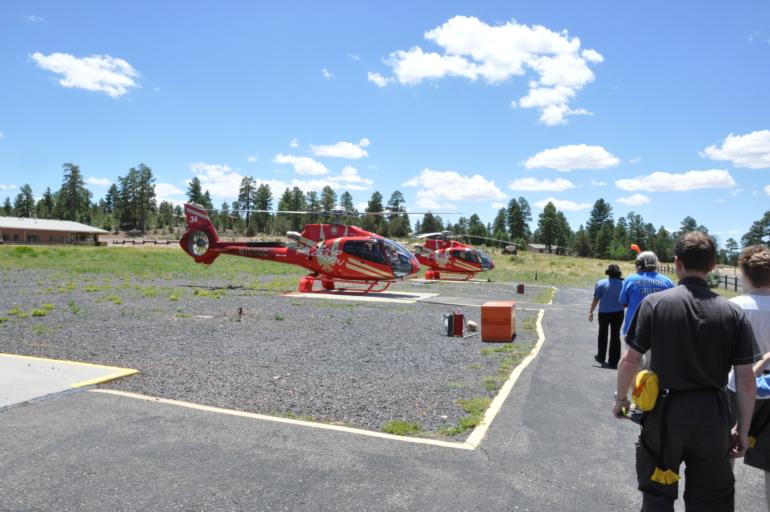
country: US
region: Arizona
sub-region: Coconino County
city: Grand Canyon Village
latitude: 35.9594
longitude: -112.1336
